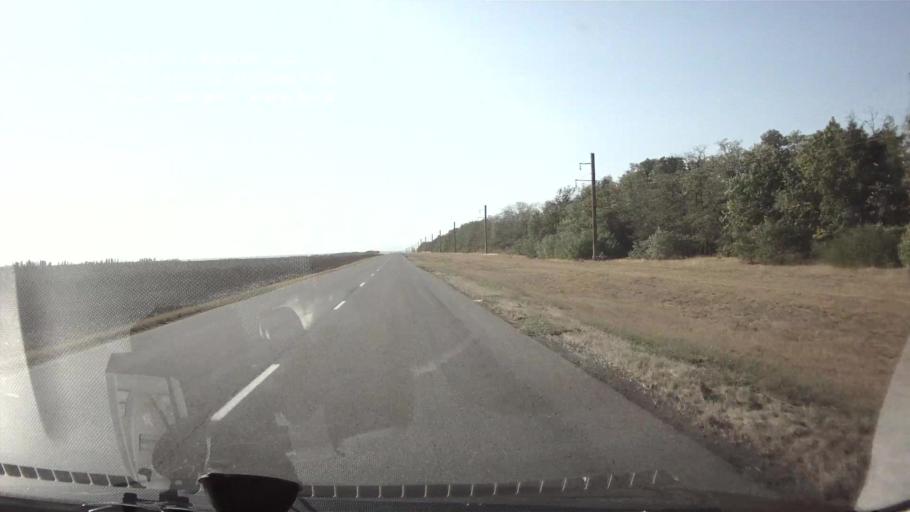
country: RU
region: Rostov
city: Tselina
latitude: 46.5121
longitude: 40.8995
